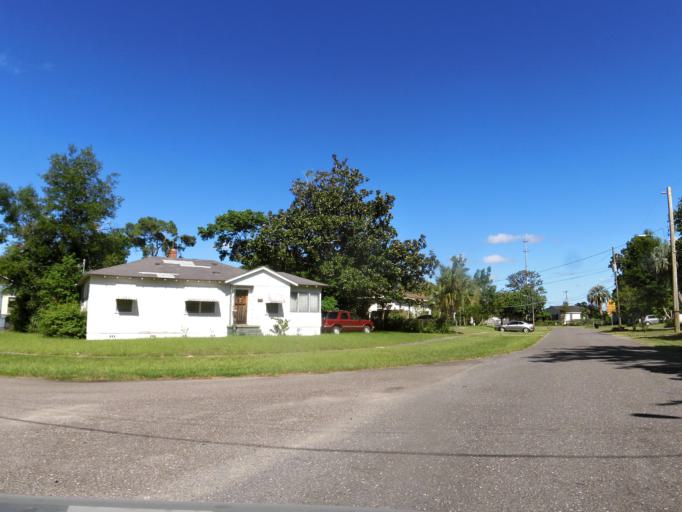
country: US
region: Florida
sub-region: Duval County
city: Jacksonville
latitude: 30.2735
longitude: -81.7276
